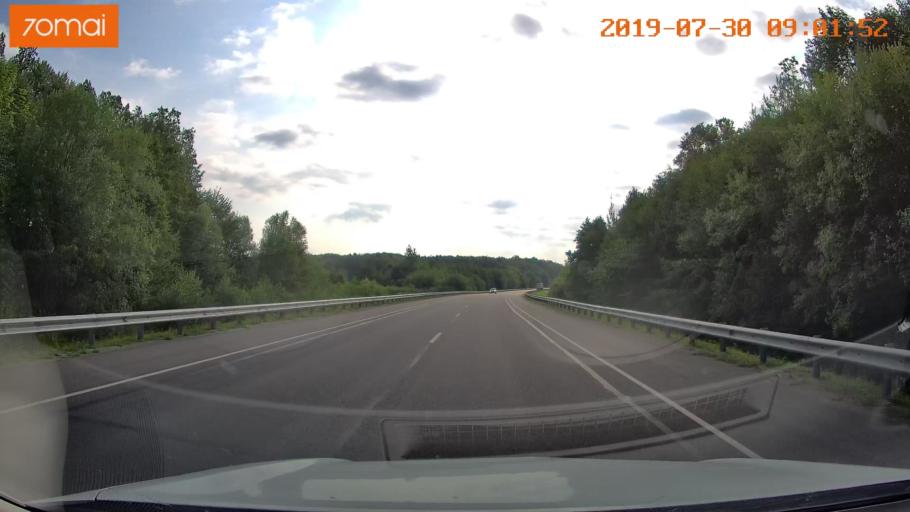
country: RU
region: Kaliningrad
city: Gusev
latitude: 54.6176
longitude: 22.2171
